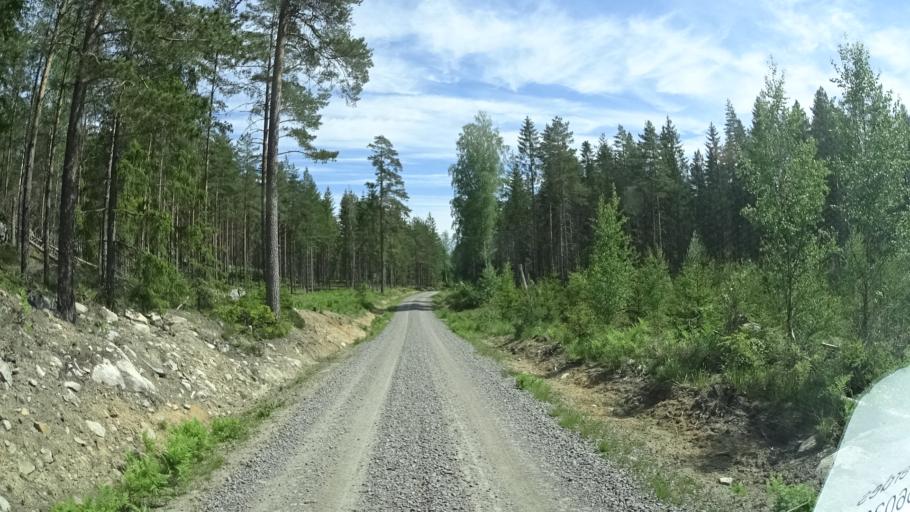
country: SE
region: OEstergoetland
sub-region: Norrkopings Kommun
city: Svartinge
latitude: 58.7711
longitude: 15.9357
